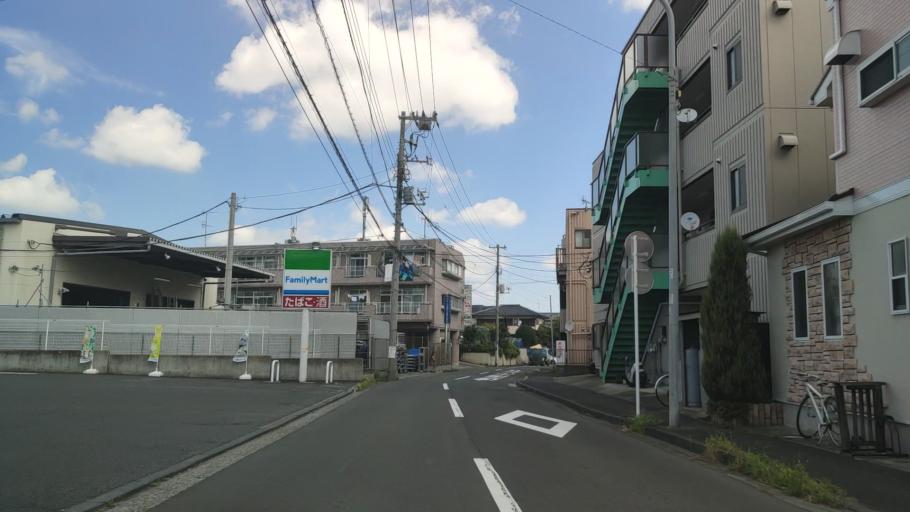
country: JP
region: Kanagawa
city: Yokohama
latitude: 35.5326
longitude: 139.6200
